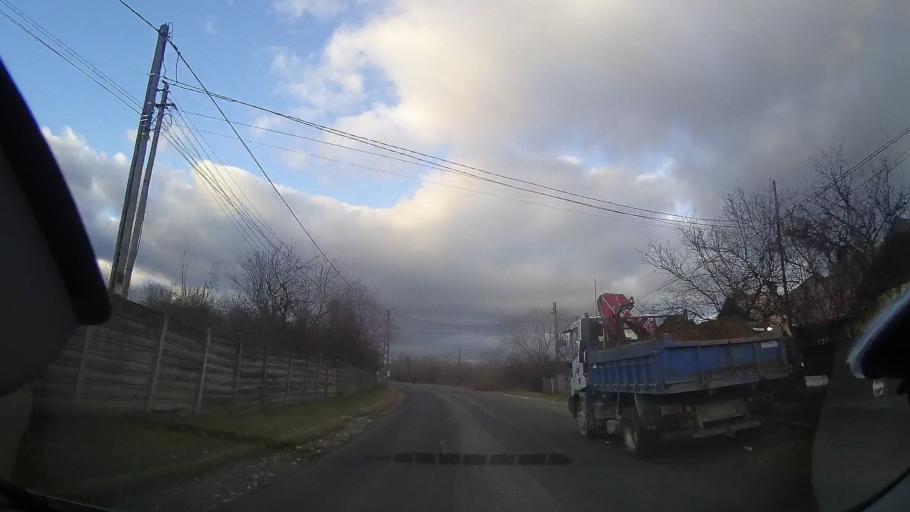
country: RO
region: Cluj
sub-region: Comuna Calatele
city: Calatele
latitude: 46.7691
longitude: 23.0084
